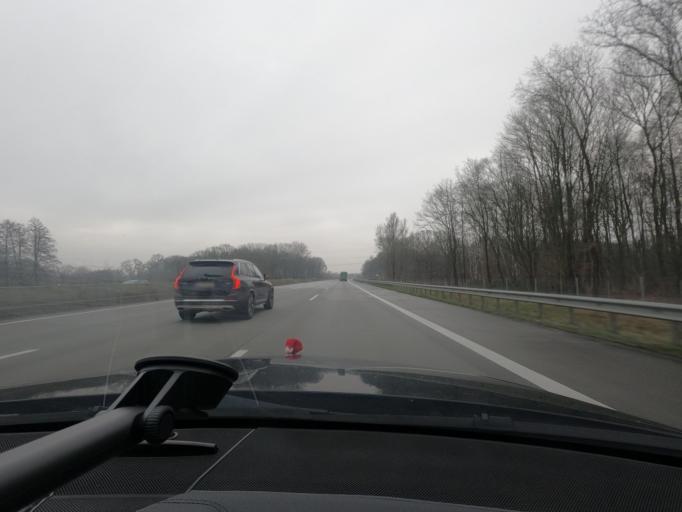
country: DE
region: Schleswig-Holstein
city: Norderstedt
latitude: 53.6888
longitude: 9.9458
